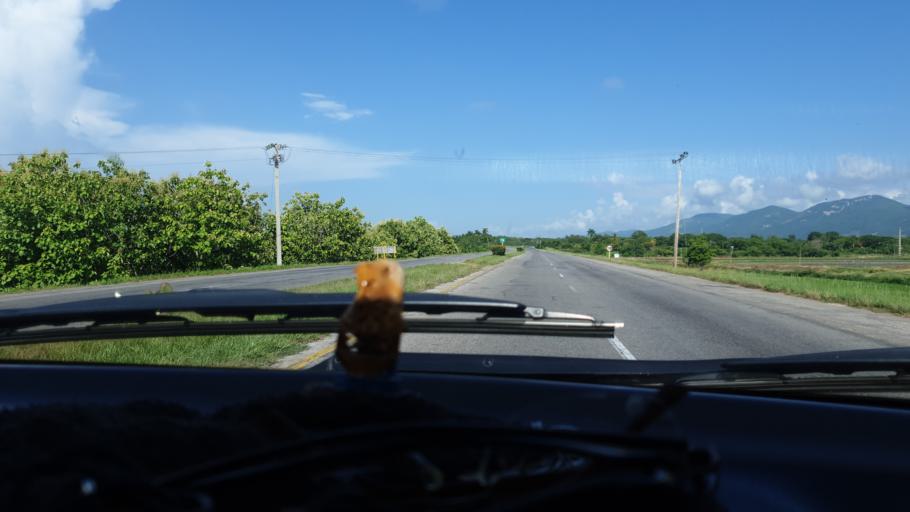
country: CU
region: Artemisa
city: San Cristobal
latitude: 22.7217
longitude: -83.0445
